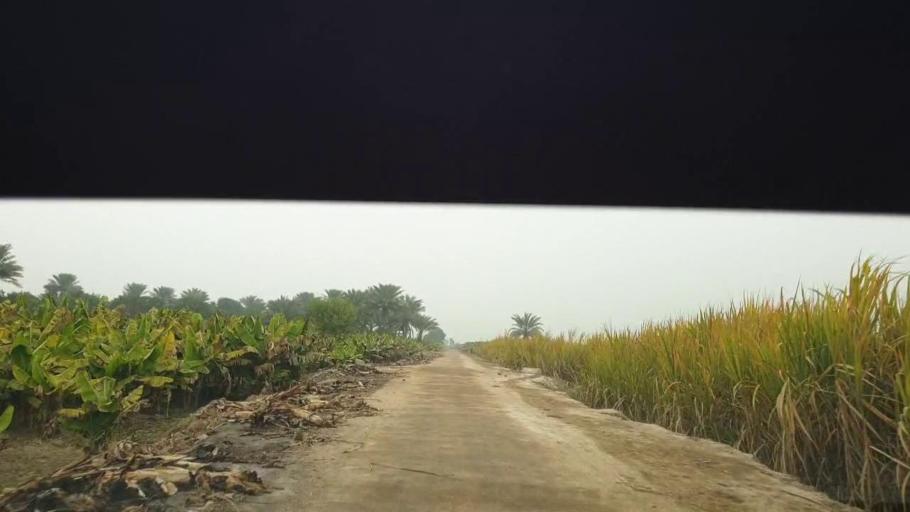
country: PK
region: Sindh
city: Tando Adam
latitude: 25.7784
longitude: 68.7319
